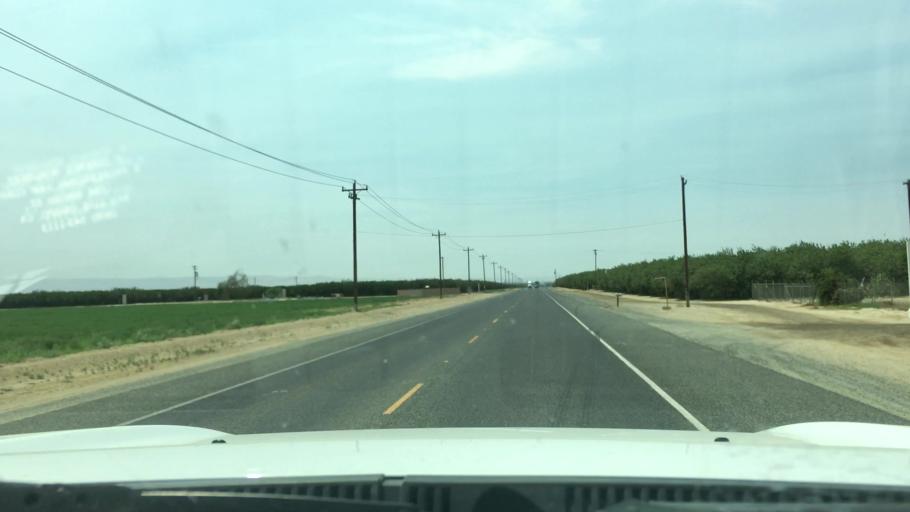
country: US
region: California
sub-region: Kern County
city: Lost Hills
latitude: 35.6012
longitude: -119.5598
